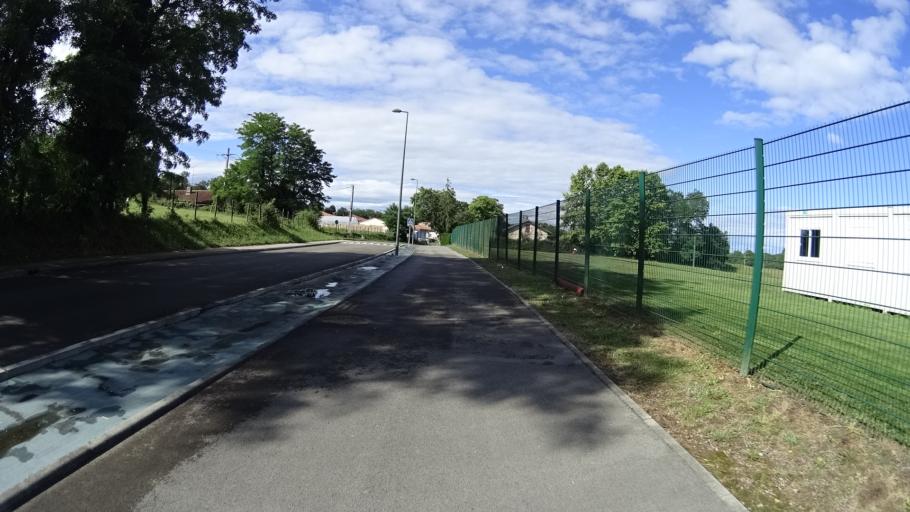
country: FR
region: Aquitaine
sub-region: Departement des Landes
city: Oeyreluy
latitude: 43.6929
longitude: -1.0821
